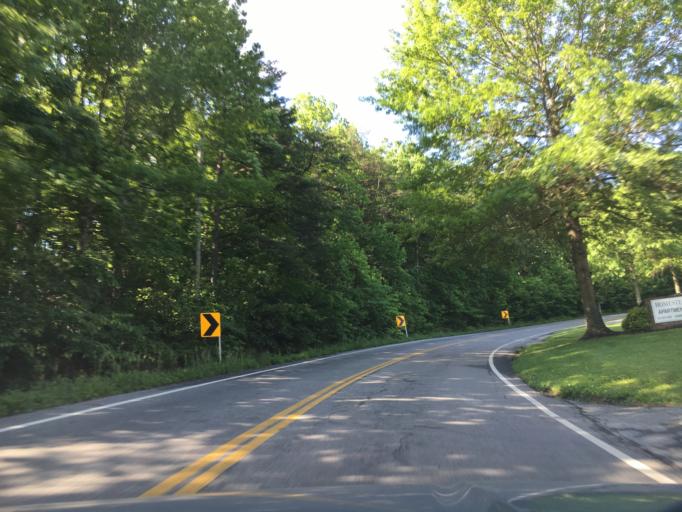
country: US
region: Virginia
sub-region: Campbell County
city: Rustburg
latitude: 37.3089
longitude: -79.1562
